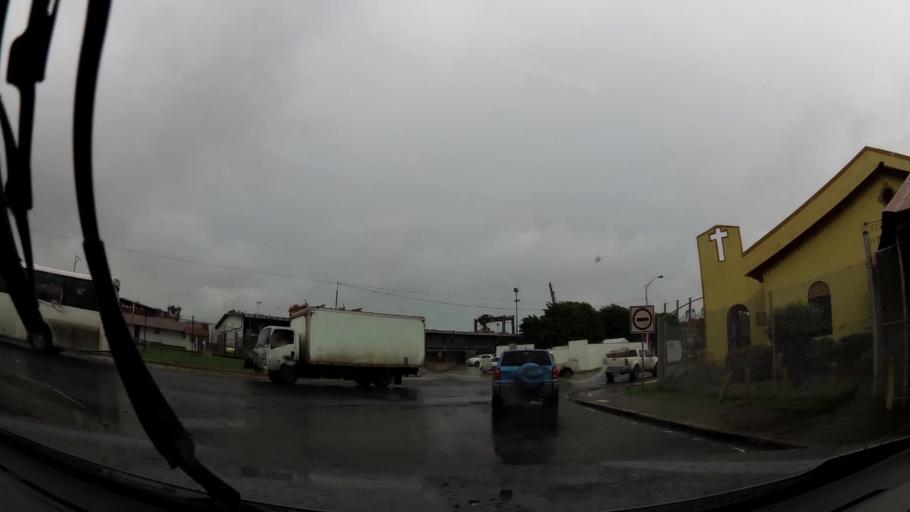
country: PA
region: Colon
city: Colon
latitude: 9.3509
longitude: -79.9001
